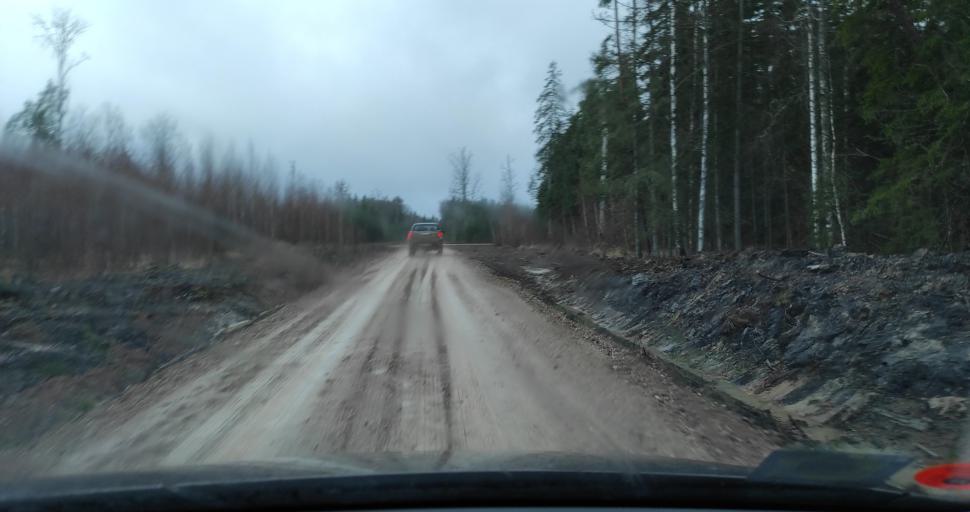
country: LV
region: Skrunda
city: Skrunda
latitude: 56.5602
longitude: 22.0596
